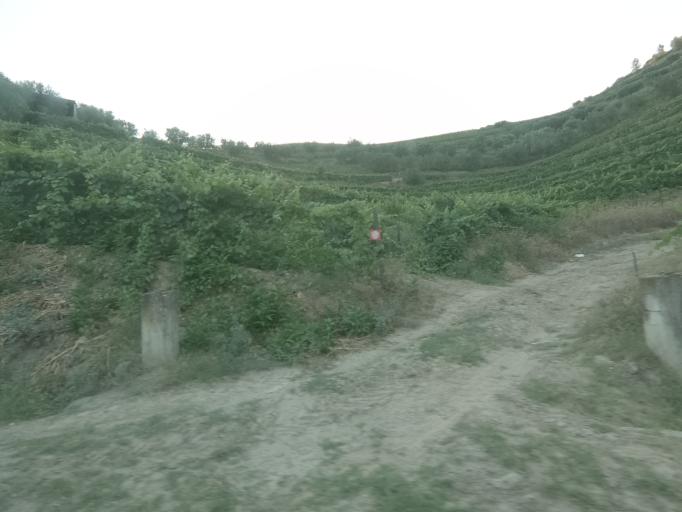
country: PT
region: Viseu
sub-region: Armamar
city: Armamar
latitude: 41.1737
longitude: -7.6883
